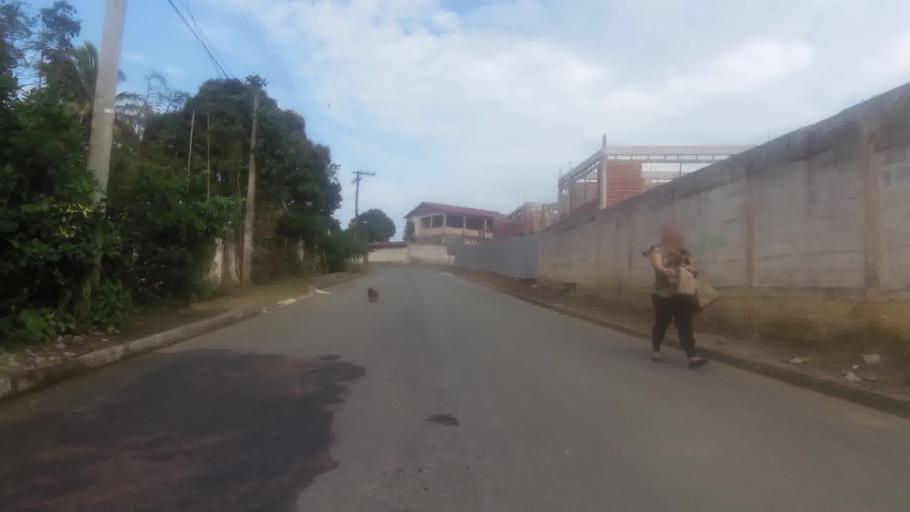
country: BR
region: Espirito Santo
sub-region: Guarapari
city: Guarapari
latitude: -20.7638
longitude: -40.5764
